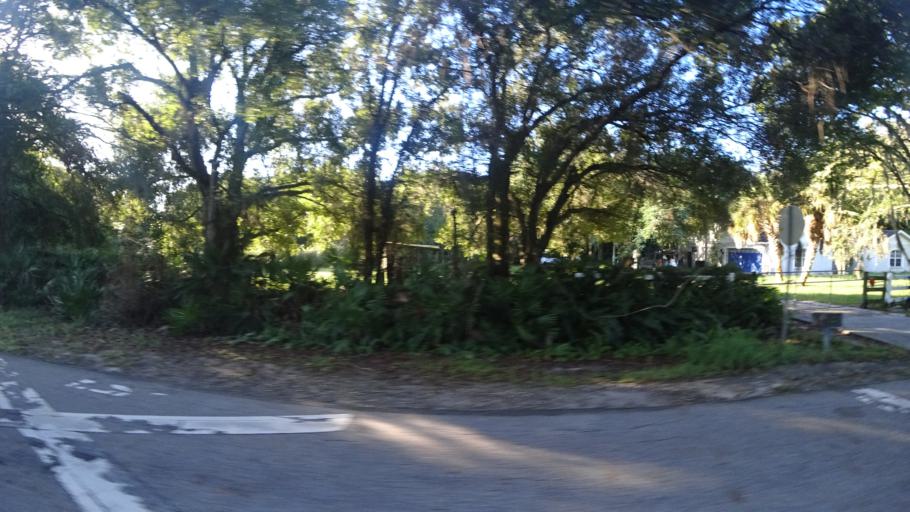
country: US
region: Florida
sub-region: Manatee County
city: Ellenton
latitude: 27.5470
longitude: -82.5334
